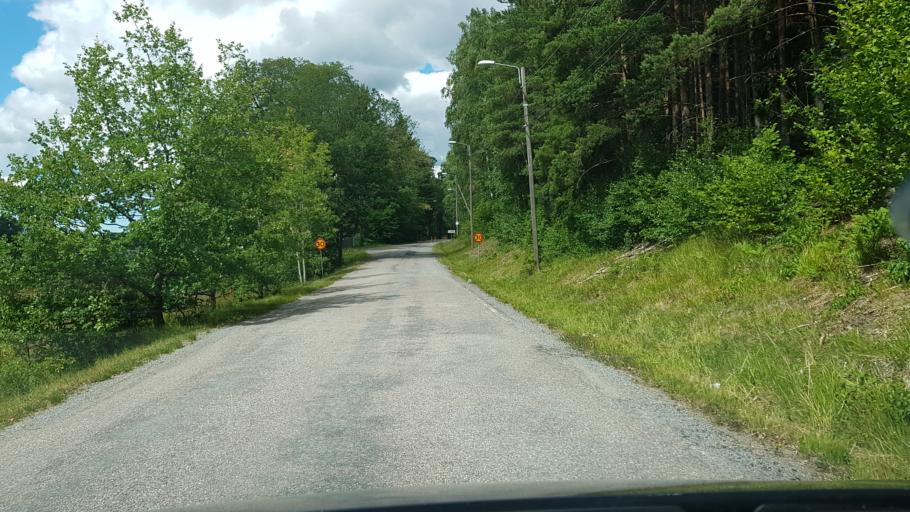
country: SE
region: Stockholm
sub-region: Upplands-Bro Kommun
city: Kungsaengen
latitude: 59.4902
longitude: 17.8042
